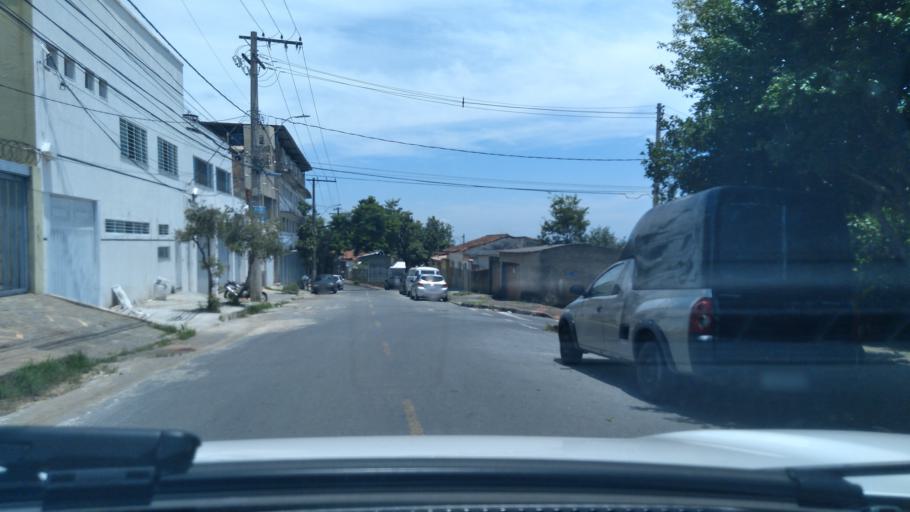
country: BR
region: Minas Gerais
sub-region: Contagem
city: Contagem
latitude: -19.9258
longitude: -44.0152
